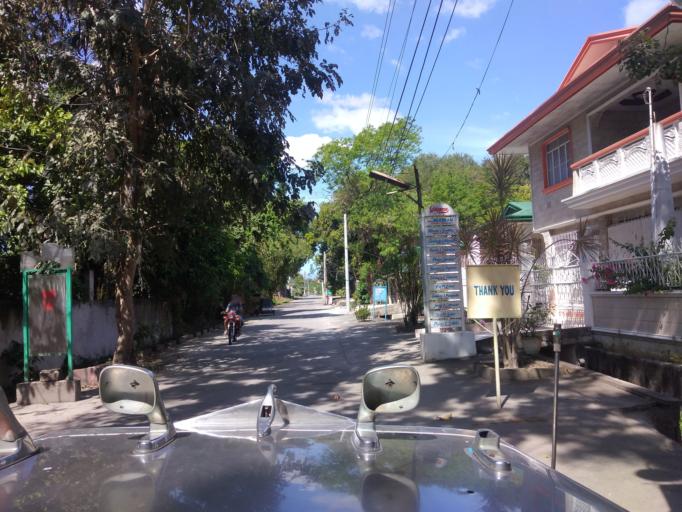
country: PH
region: Central Luzon
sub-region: Province of Pampanga
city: Santa Rita
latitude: 15.0042
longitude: 120.6004
